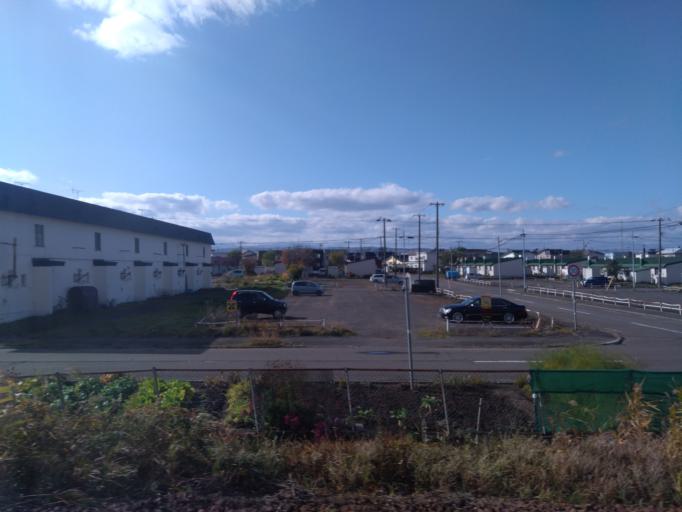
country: JP
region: Hokkaido
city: Kitahiroshima
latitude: 42.8984
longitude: 141.5748
